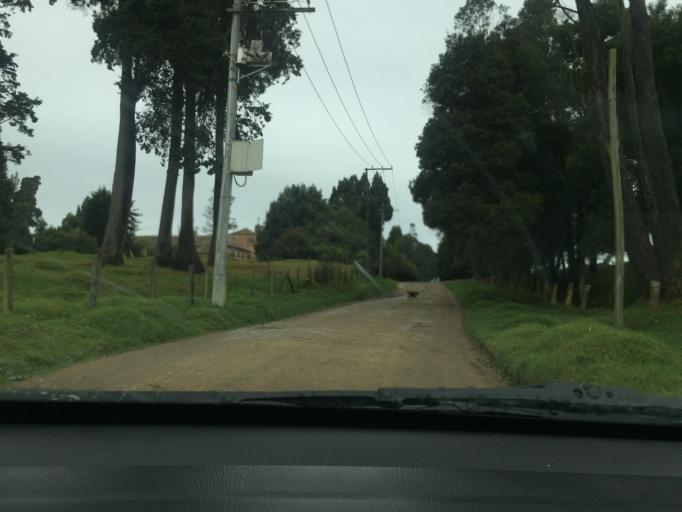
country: CO
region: Cundinamarca
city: Madrid
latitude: 4.7910
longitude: -74.2767
